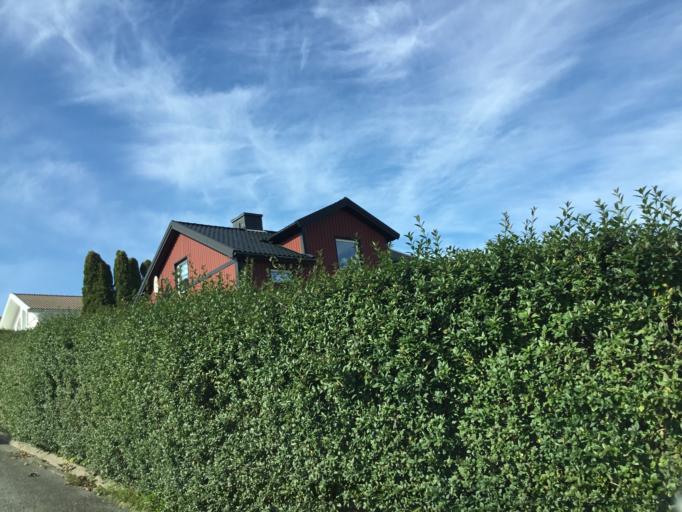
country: SE
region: Vaestra Goetaland
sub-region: Molndal
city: Moelndal
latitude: 57.6603
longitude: 12.0411
